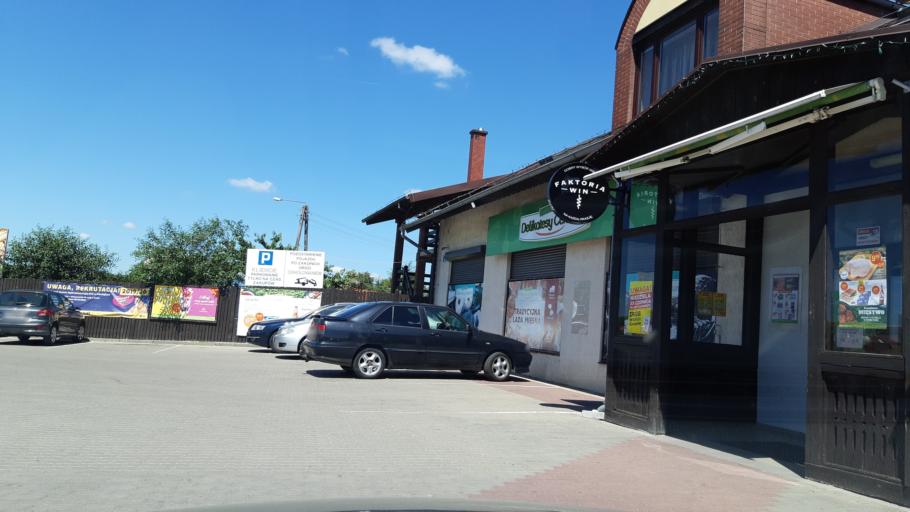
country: PL
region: Warmian-Masurian Voivodeship
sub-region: Powiat mragowski
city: Mikolajki
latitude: 53.8015
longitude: 21.5758
